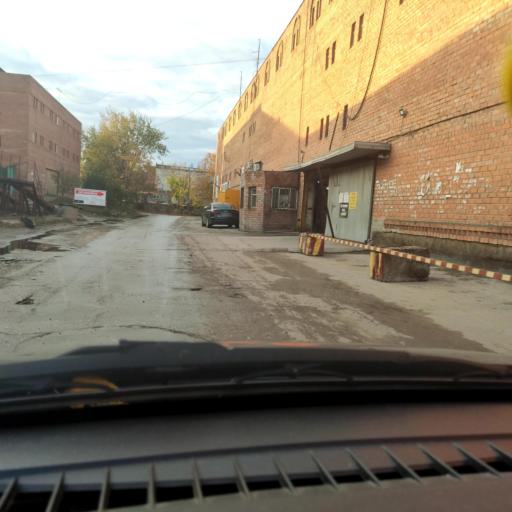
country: RU
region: Samara
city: Tol'yatti
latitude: 53.5392
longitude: 49.2900
